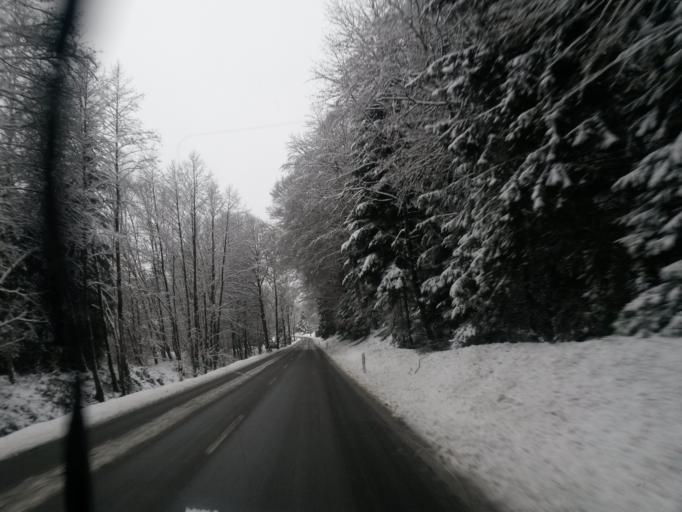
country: DE
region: Baden-Wuerttemberg
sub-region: Karlsruhe Region
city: Bad Wildbad
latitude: 48.7090
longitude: 8.5417
